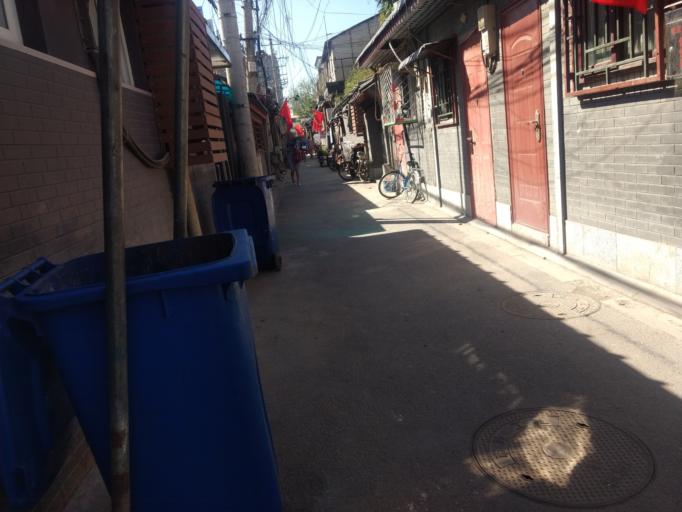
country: CN
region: Beijing
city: Beijing
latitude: 39.8890
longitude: 116.3825
